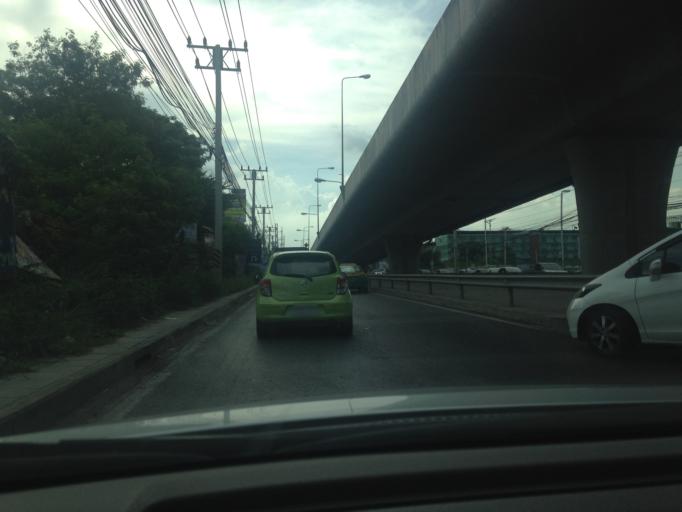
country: TH
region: Pathum Thani
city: Khlong Luang
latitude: 14.0652
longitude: 100.6340
